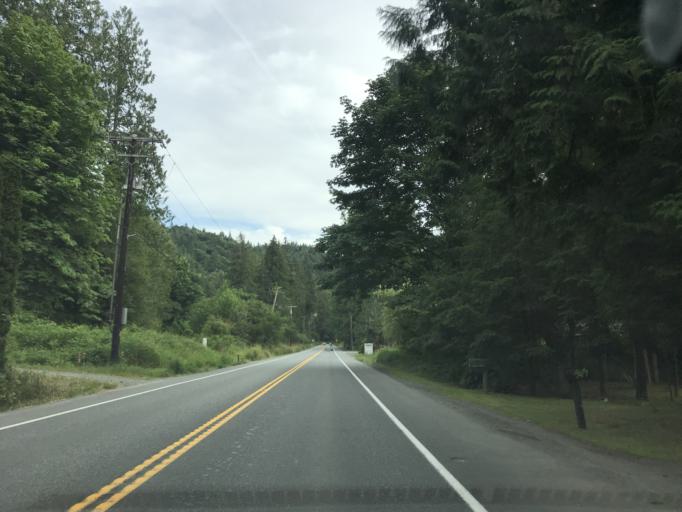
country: US
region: Washington
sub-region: King County
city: Fall City
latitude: 47.5524
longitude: -121.8998
